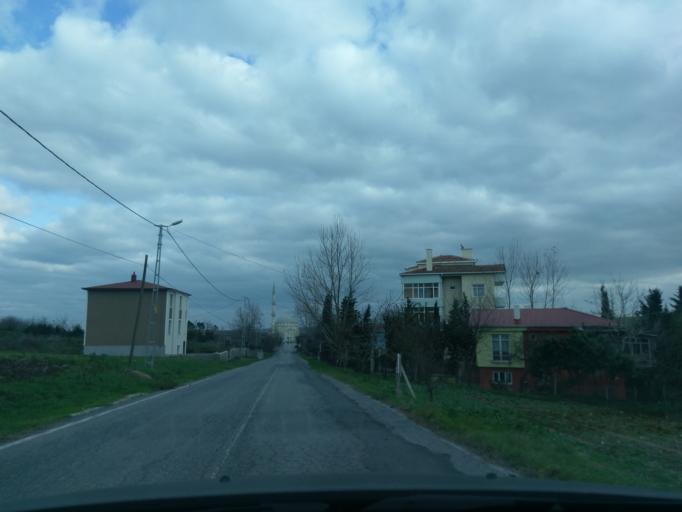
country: TR
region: Istanbul
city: Boyalik
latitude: 41.2718
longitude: 28.6588
